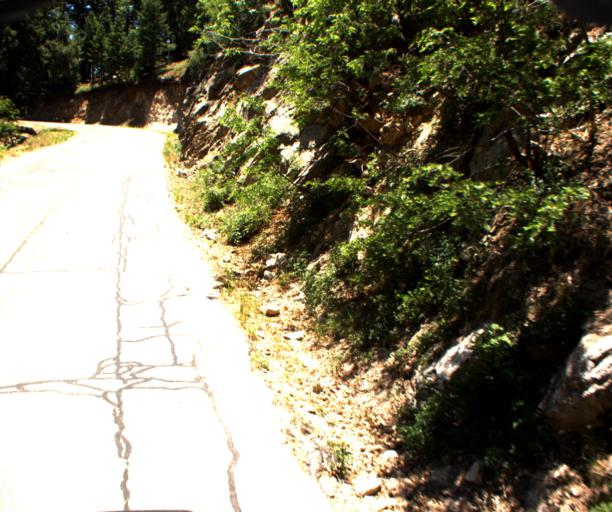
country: US
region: Arizona
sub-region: Graham County
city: Swift Trail Junction
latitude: 32.6229
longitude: -109.8254
